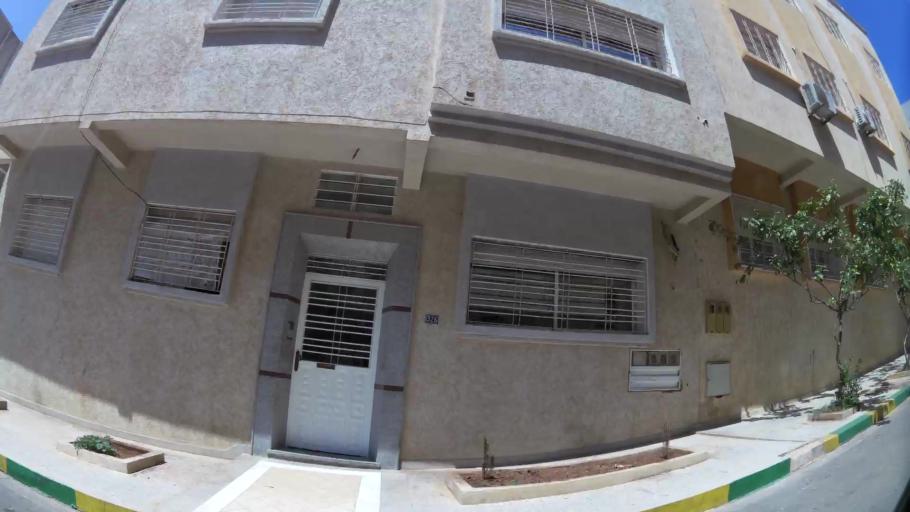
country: MA
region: Fes-Boulemane
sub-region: Fes
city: Fes
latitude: 34.0614
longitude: -5.0274
